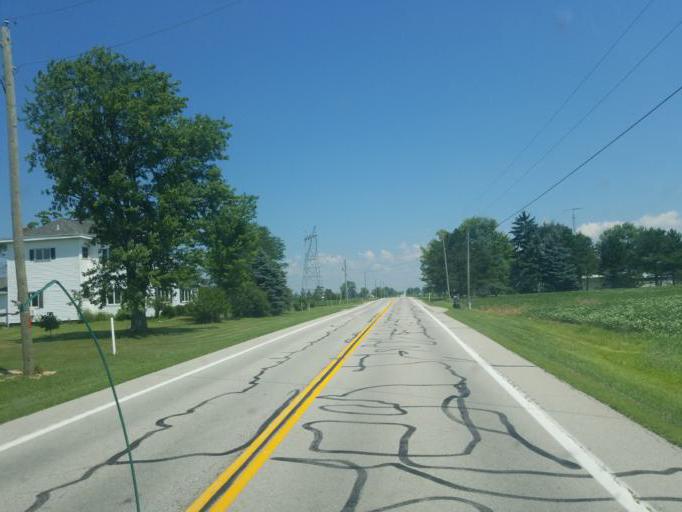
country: US
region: Ohio
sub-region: Shelby County
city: Anna
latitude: 40.3956
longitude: -84.1103
